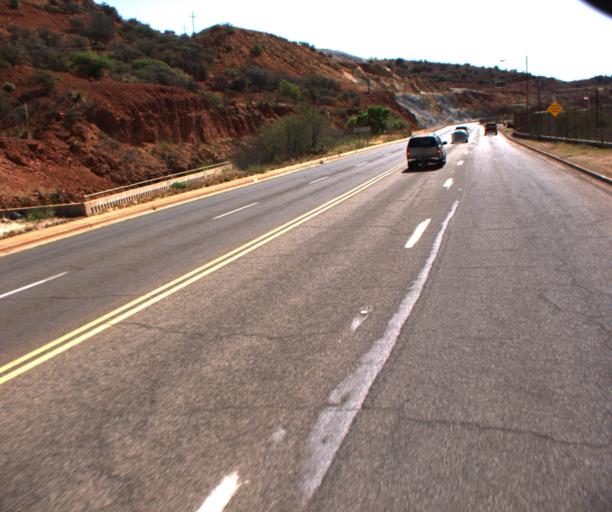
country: US
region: Arizona
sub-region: Cochise County
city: Bisbee
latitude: 31.4364
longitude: -109.9027
